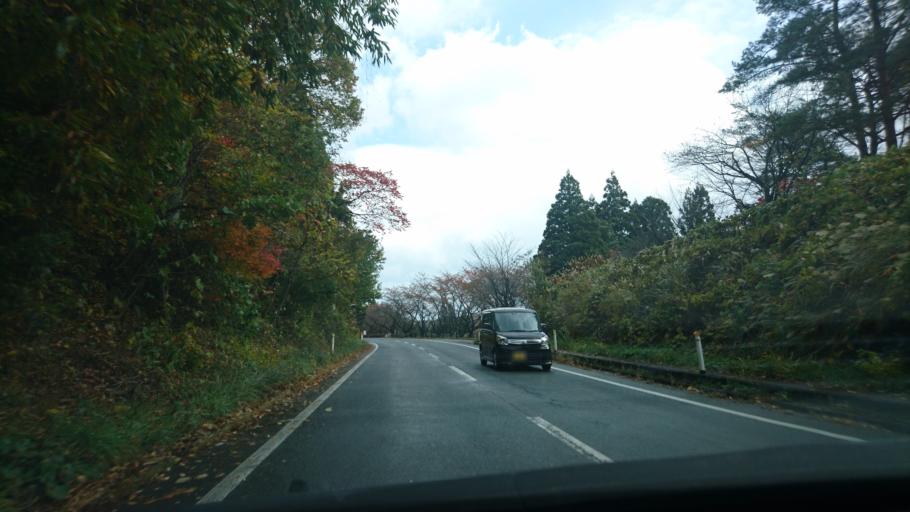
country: JP
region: Iwate
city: Shizukuishi
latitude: 39.6852
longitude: 141.0203
